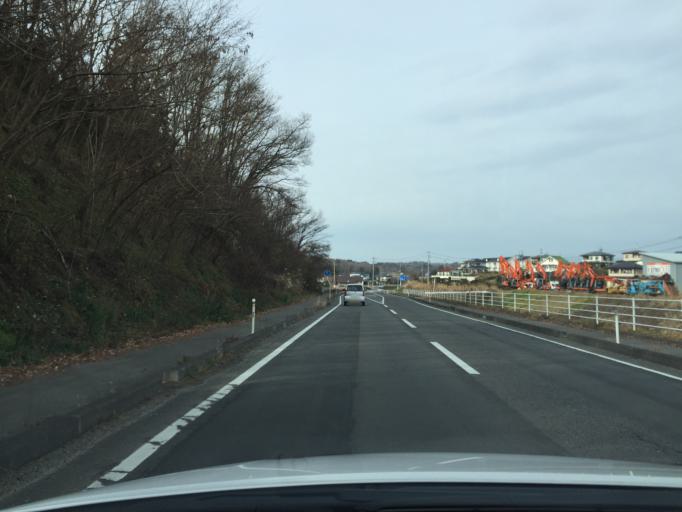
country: JP
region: Fukushima
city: Funehikimachi-funehiki
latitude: 37.4527
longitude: 140.5780
